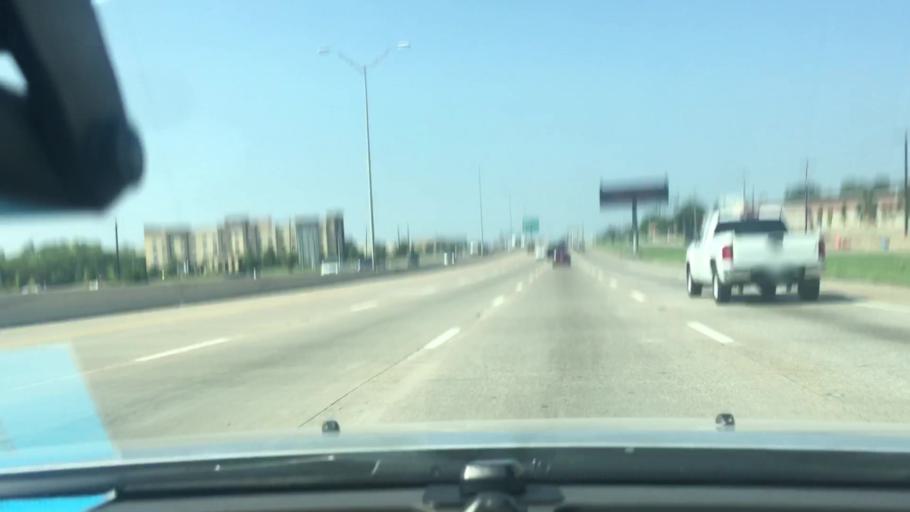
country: US
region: Texas
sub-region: Dallas County
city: DeSoto
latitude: 32.6242
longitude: -96.8224
